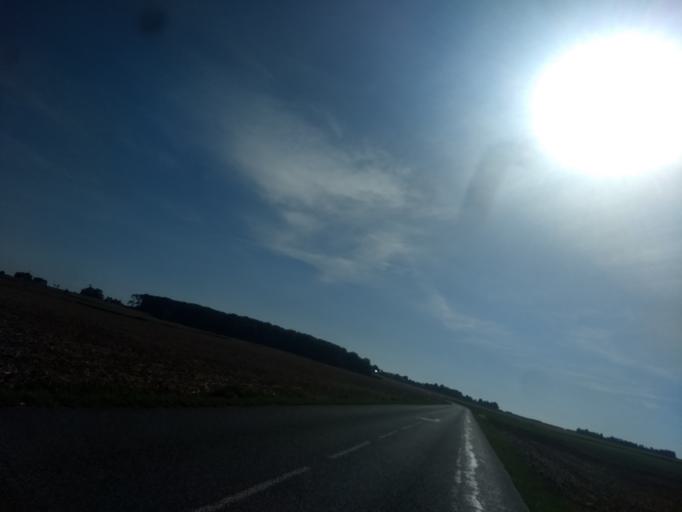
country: FR
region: Nord-Pas-de-Calais
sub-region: Departement du Pas-de-Calais
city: Roeux
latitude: 50.2819
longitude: 2.8992
